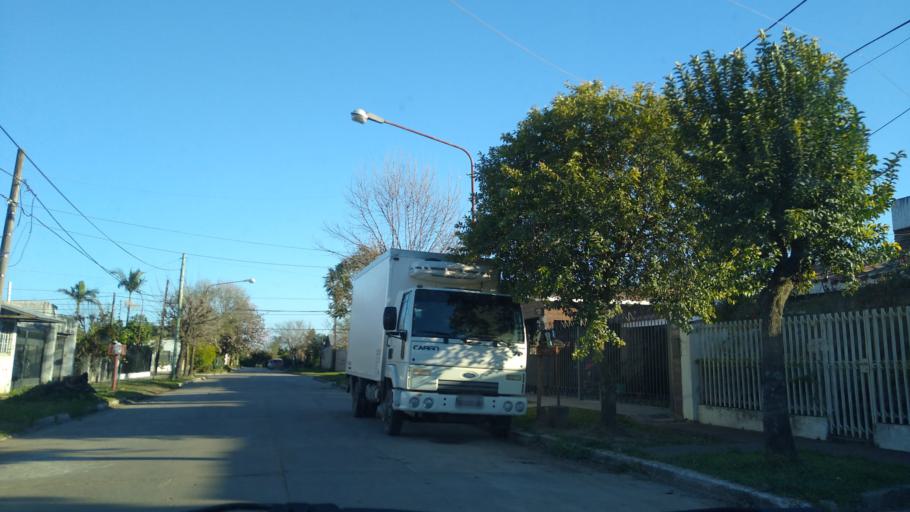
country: AR
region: Chaco
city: Barranqueras
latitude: -27.4804
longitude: -58.9488
